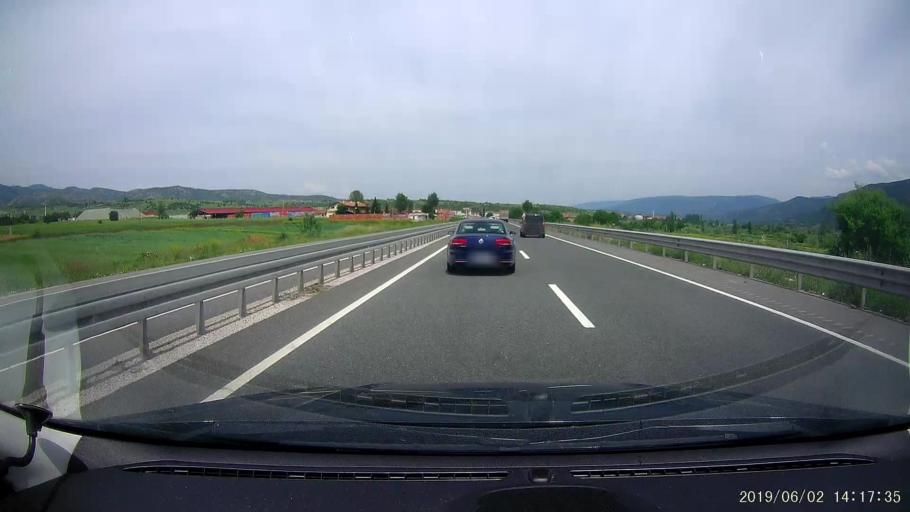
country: TR
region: Kastamonu
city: Tosya
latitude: 40.9547
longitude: 33.9358
